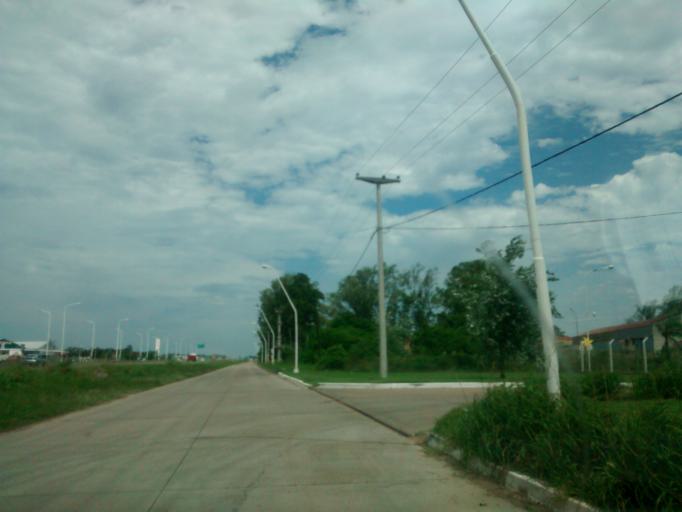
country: AR
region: Chaco
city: Fontana
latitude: -27.4099
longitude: -58.9795
